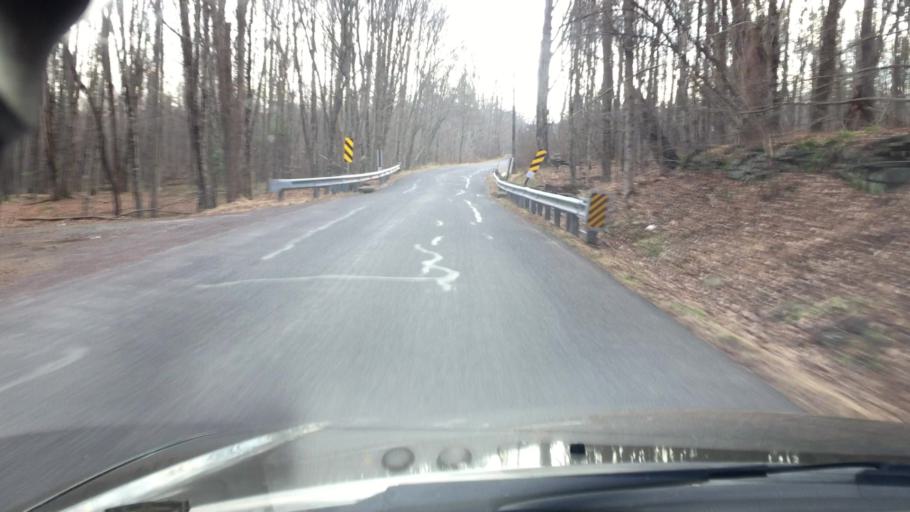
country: US
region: Pennsylvania
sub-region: Luzerne County
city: Back Mountain
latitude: 41.2948
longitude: -76.0475
